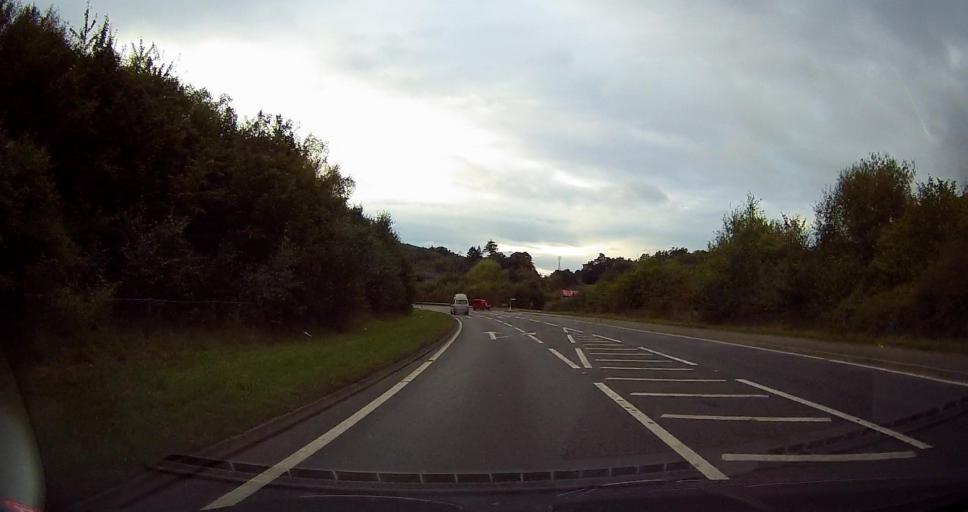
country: GB
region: England
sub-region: Kent
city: Harrietsham
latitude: 51.2488
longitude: 0.6475
